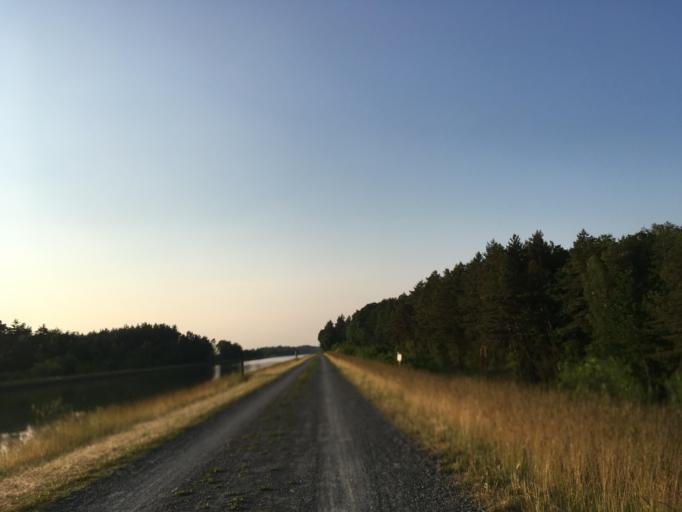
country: DE
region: Lower Saxony
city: Wendisch Evern
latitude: 53.2543
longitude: 10.4866
